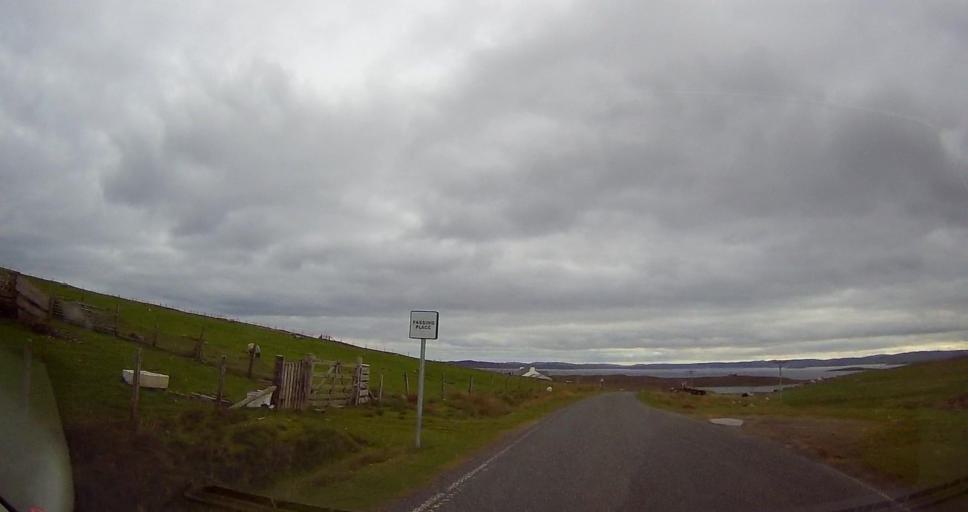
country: GB
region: Scotland
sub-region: Shetland Islands
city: Shetland
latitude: 60.5075
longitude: -1.0587
